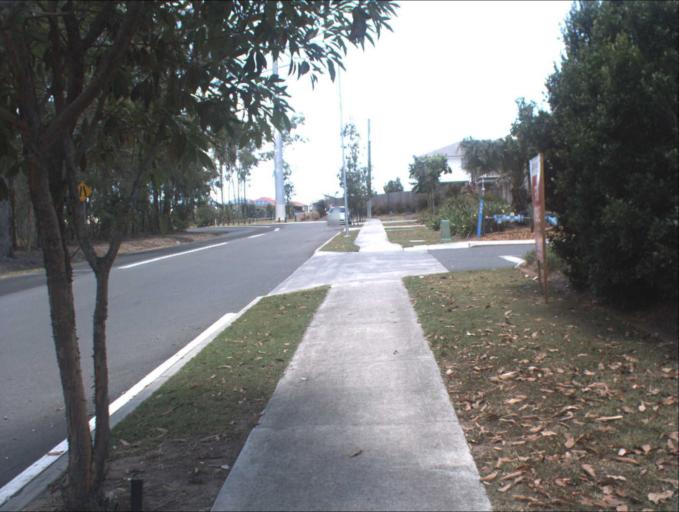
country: AU
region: Queensland
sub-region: Logan
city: Woodridge
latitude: -27.6596
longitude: 153.0877
